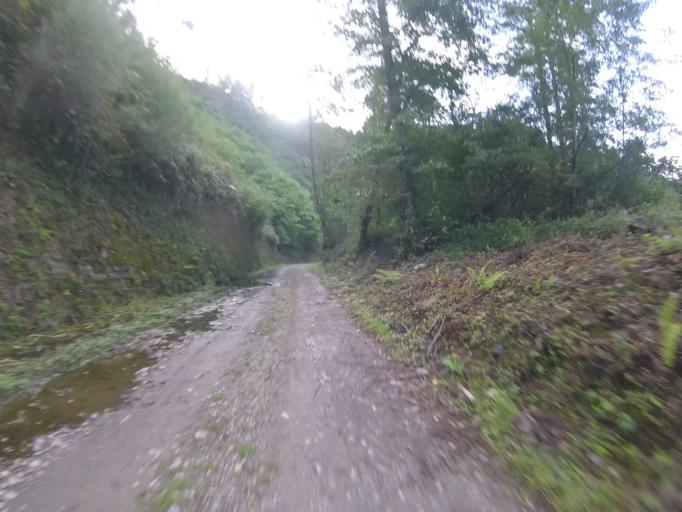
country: ES
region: Basque Country
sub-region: Provincia de Guipuzcoa
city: Berastegui
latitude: 43.1556
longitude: -1.9635
